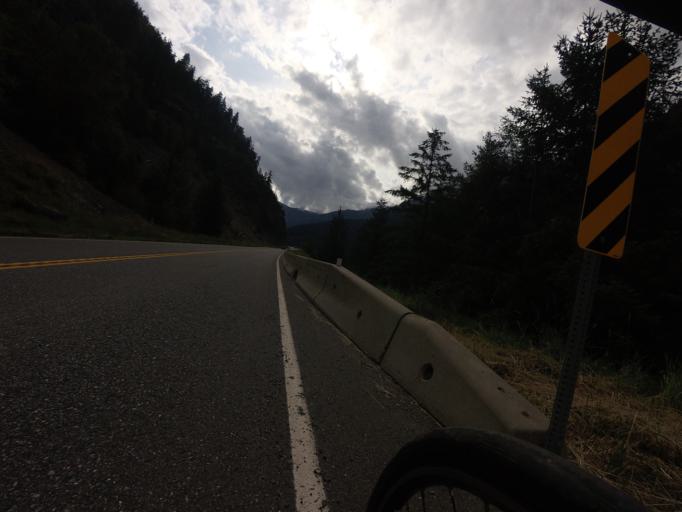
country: CA
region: British Columbia
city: Lillooet
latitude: 50.6422
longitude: -122.0448
